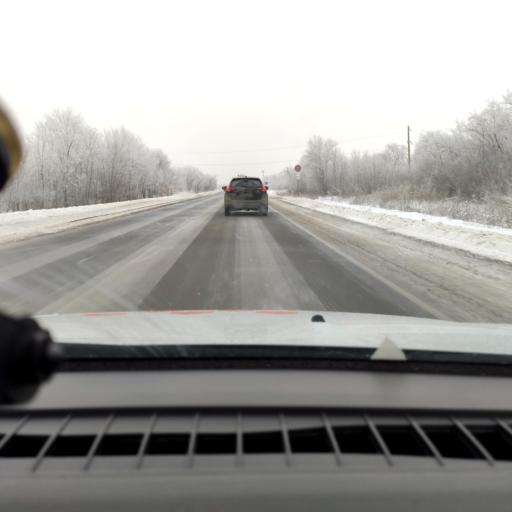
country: RU
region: Samara
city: Samara
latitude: 53.0803
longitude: 50.1641
